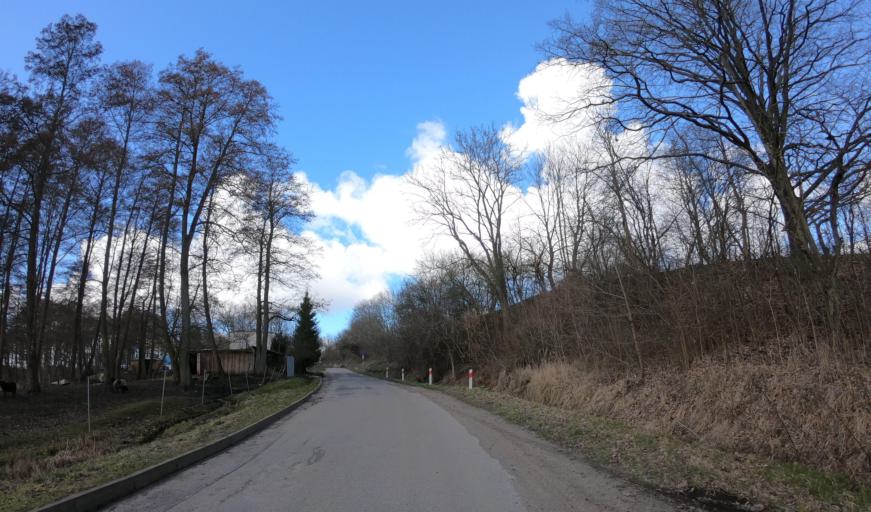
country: PL
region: West Pomeranian Voivodeship
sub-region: Powiat drawski
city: Zlocieniec
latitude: 53.4608
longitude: 15.9416
